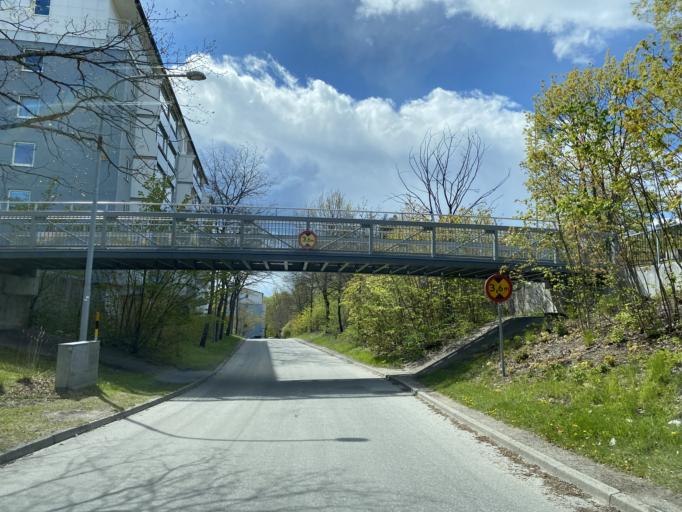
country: SE
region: Stockholm
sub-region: Stockholms Kommun
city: Kista
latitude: 59.4070
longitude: 17.9280
